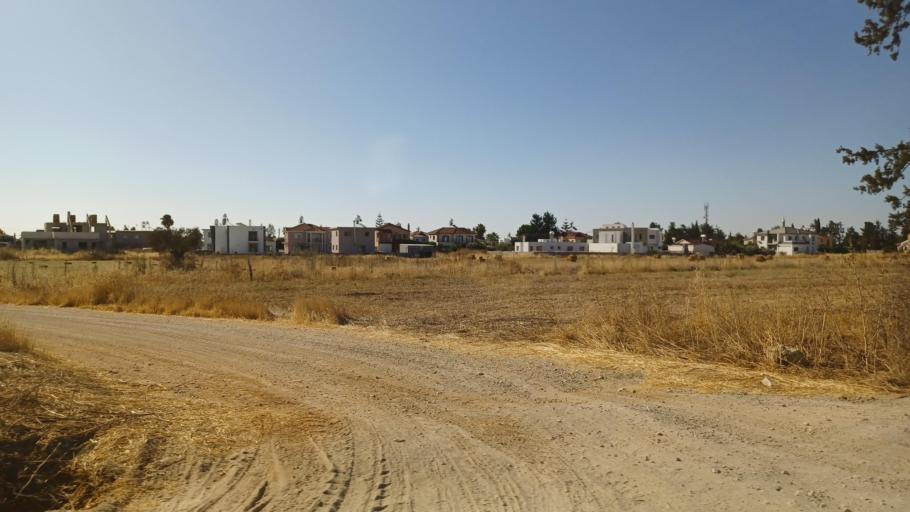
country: CY
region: Larnaka
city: Pergamos
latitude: 35.0450
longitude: 33.7040
